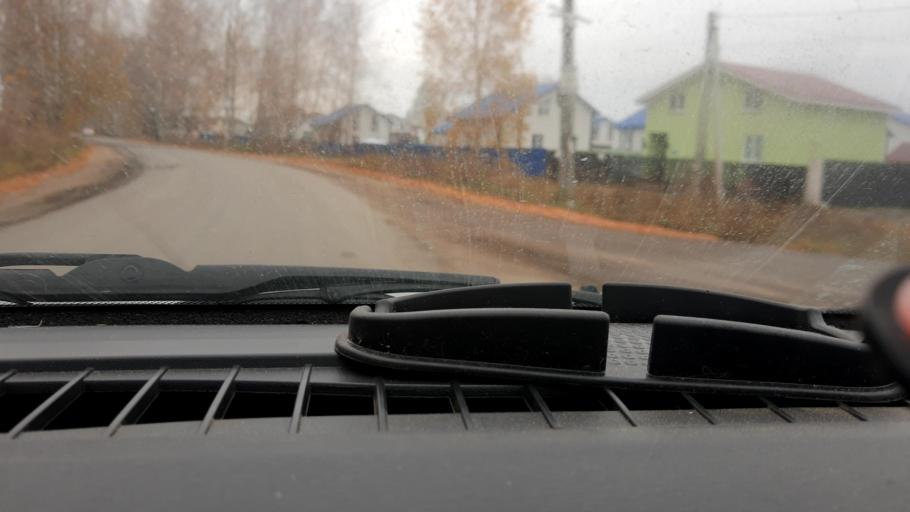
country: RU
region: Nizjnij Novgorod
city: Neklyudovo
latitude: 56.4094
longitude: 44.0273
